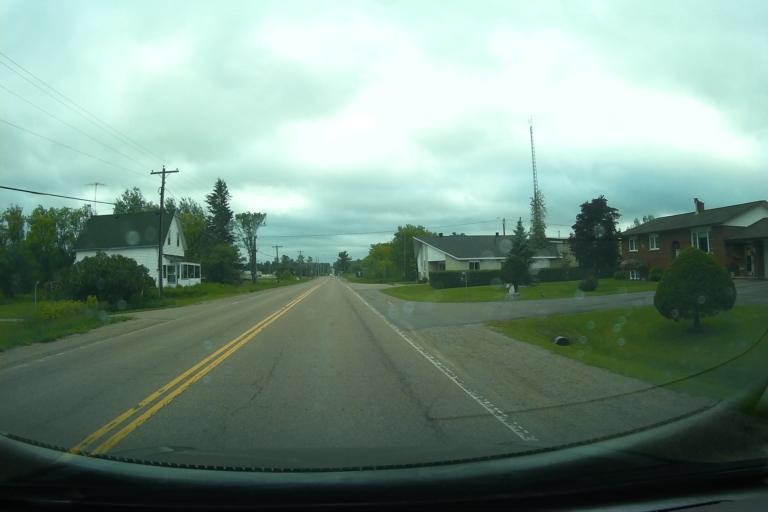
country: CA
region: Ontario
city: Pembroke
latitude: 45.5277
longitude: -77.1135
